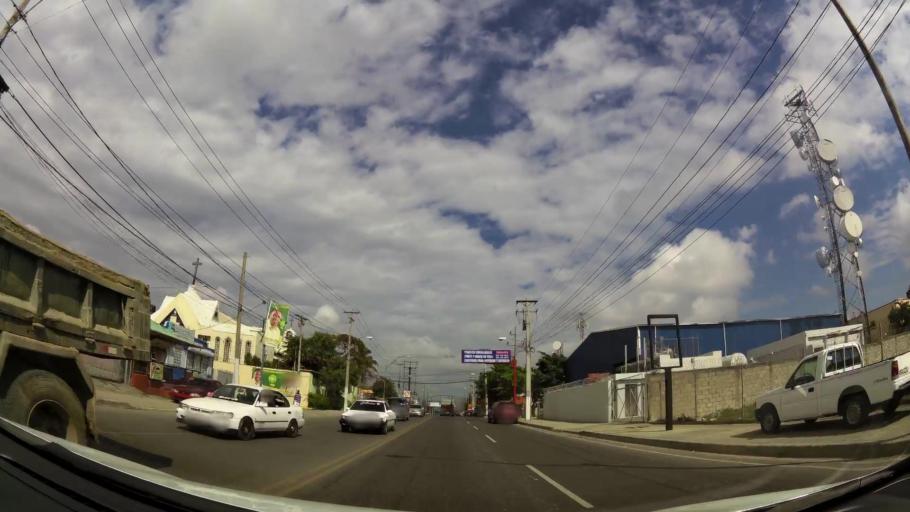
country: DO
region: Santiago
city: Santiago de los Caballeros
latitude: 19.4818
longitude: -70.7280
